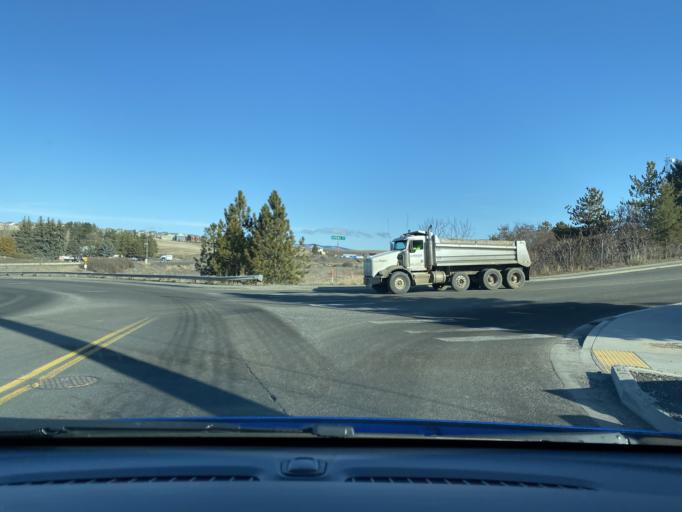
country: US
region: Washington
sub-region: Whitman County
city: Pullman
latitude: 46.7495
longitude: -117.1698
